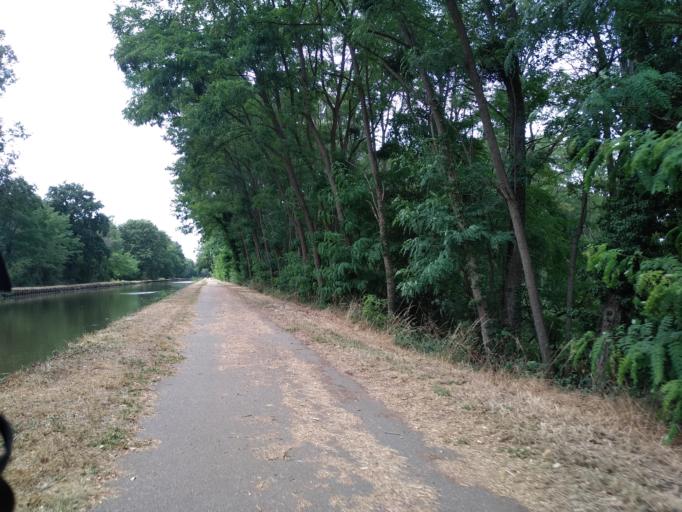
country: FR
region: Auvergne
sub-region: Departement de l'Allier
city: Diou
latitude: 46.5306
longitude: 3.7267
